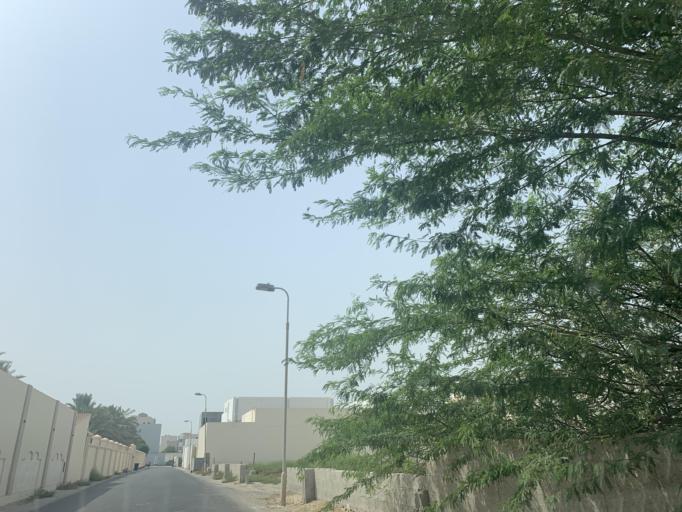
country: BH
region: Manama
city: Jidd Hafs
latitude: 26.1968
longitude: 50.4695
